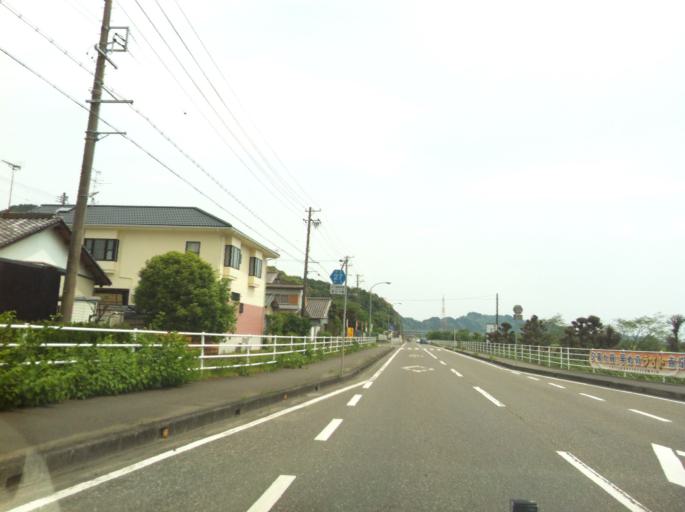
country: JP
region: Shizuoka
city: Shizuoka-shi
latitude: 35.0545
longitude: 138.3716
